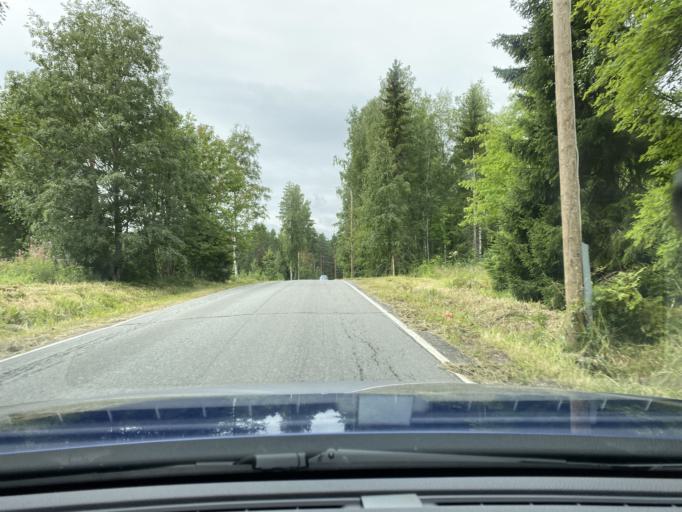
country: FI
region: Pirkanmaa
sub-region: Ylae-Pirkanmaa
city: Maenttae
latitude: 62.0260
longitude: 24.7114
